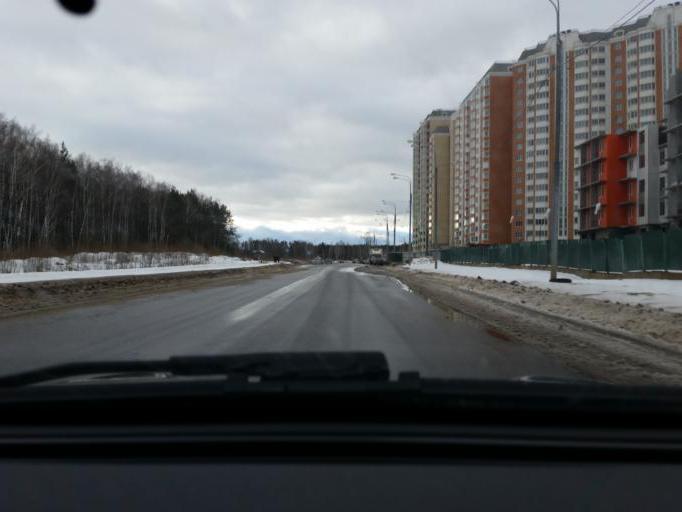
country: RU
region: Moskovskaya
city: Shcherbinka
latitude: 55.5237
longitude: 37.5996
